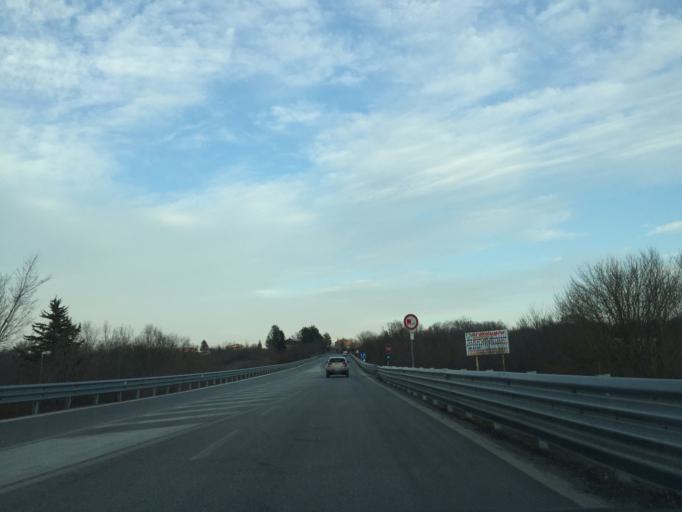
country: IT
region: Molise
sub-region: Provincia di Campobasso
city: Vinchiaturo
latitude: 41.4757
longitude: 14.5661
